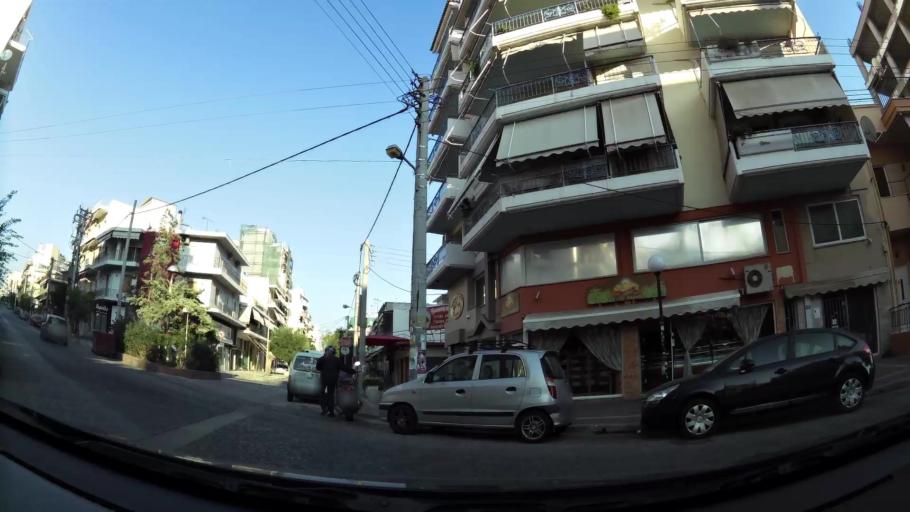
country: GR
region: Attica
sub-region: Nomos Piraios
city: Nikaia
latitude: 37.9671
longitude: 23.6372
